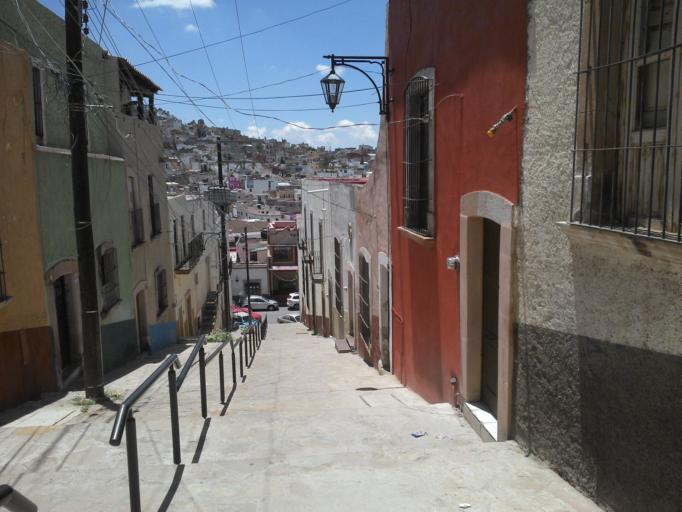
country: MX
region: Zacatecas
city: Zacatecas
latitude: 22.7777
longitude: -102.5729
